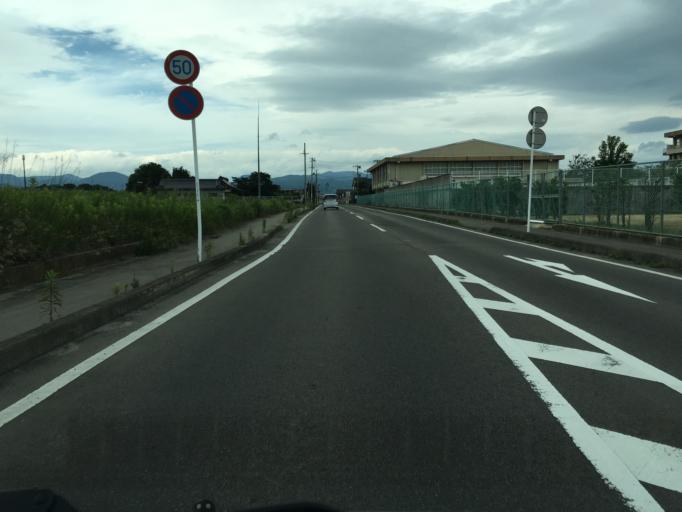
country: JP
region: Fukushima
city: Fukushima-shi
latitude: 37.7719
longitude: 140.4346
